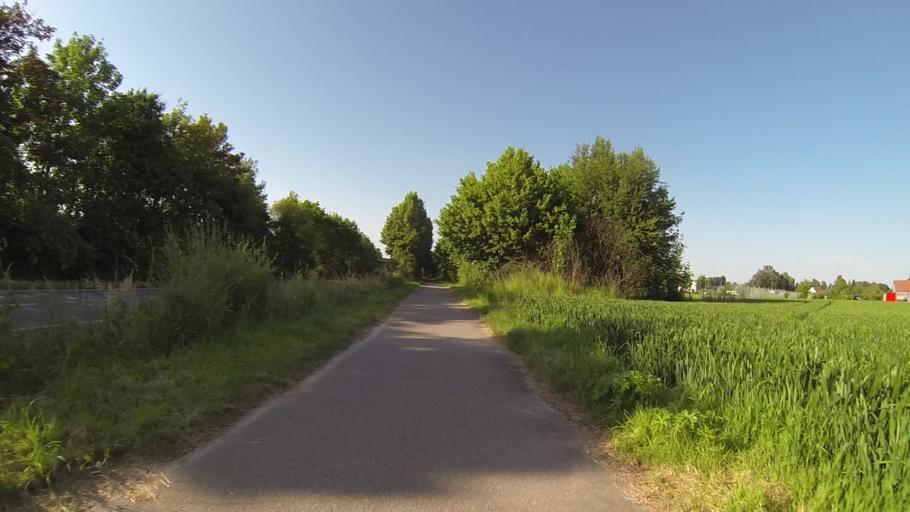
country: DE
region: Baden-Wuerttemberg
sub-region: Tuebingen Region
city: Laupheim
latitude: 48.2059
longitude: 9.8787
